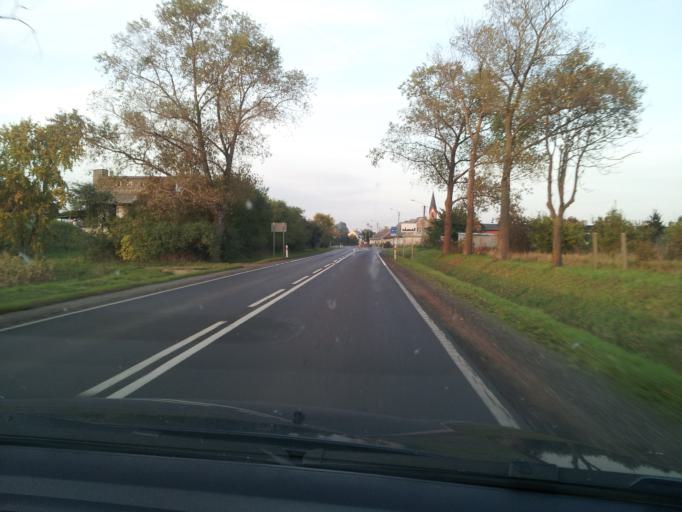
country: PL
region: Kujawsko-Pomorskie
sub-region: Powiat inowroclawski
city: Wierzchoslawice
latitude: 52.8425
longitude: 18.3299
